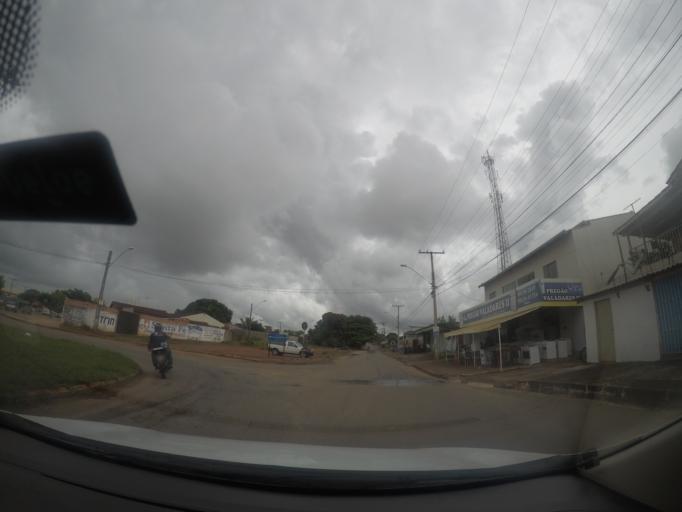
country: BR
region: Goias
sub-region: Trindade
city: Trindade
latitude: -16.6465
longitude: -49.3891
